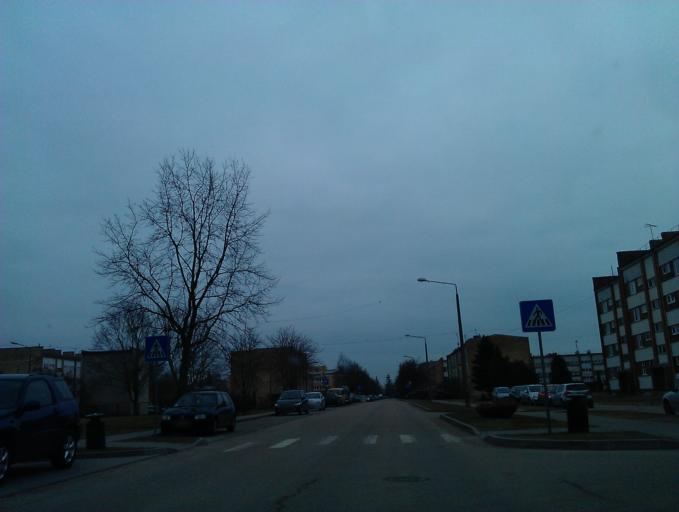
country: LV
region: Adazi
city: Adazi
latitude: 57.0808
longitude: 24.3211
